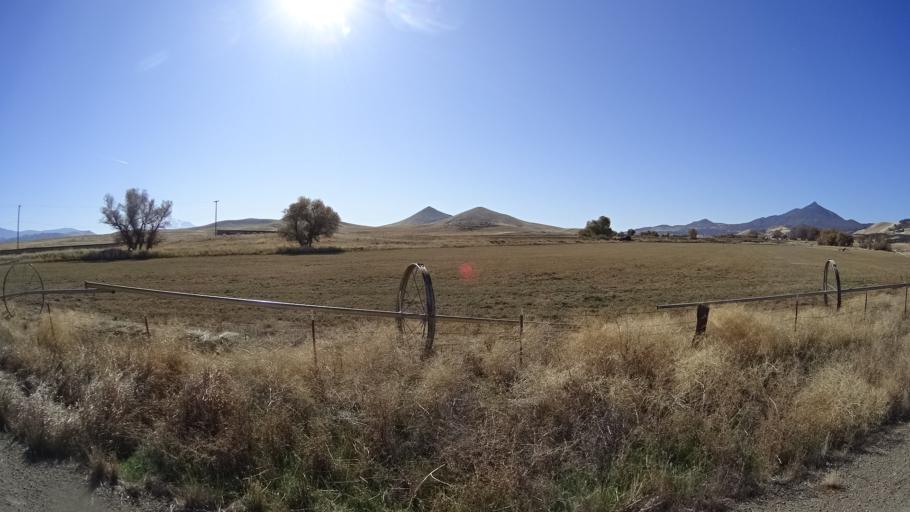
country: US
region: California
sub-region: Siskiyou County
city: Montague
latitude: 41.8480
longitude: -122.4665
